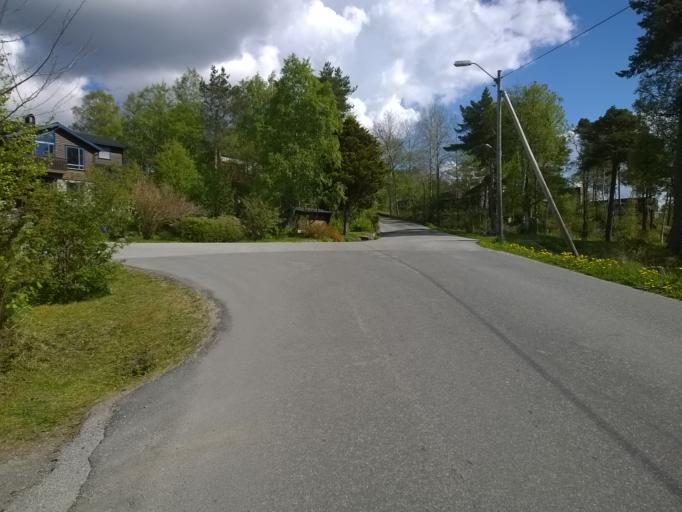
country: NO
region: More og Romsdal
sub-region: Molde
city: Molde
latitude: 62.7373
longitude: 7.1307
